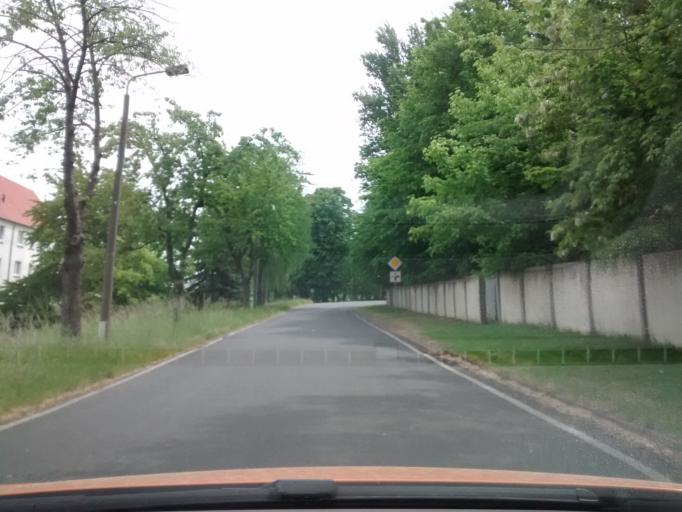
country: DE
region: Brandenburg
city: Juterbog
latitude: 51.9845
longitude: 13.0719
